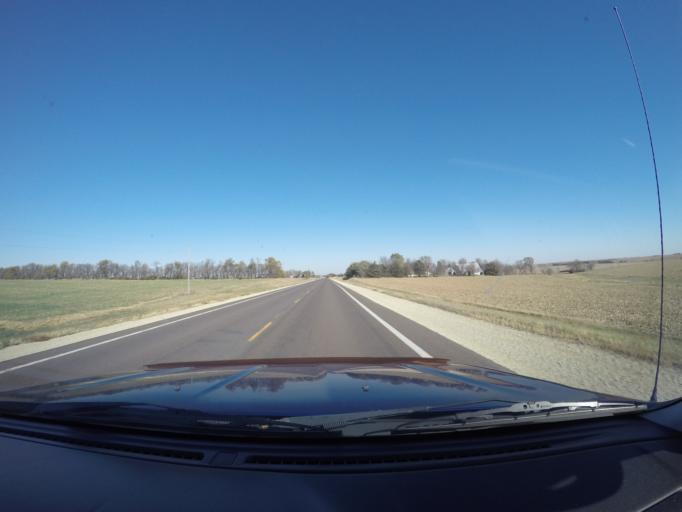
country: US
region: Kansas
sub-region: Marshall County
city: Blue Rapids
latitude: 39.6014
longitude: -96.7501
